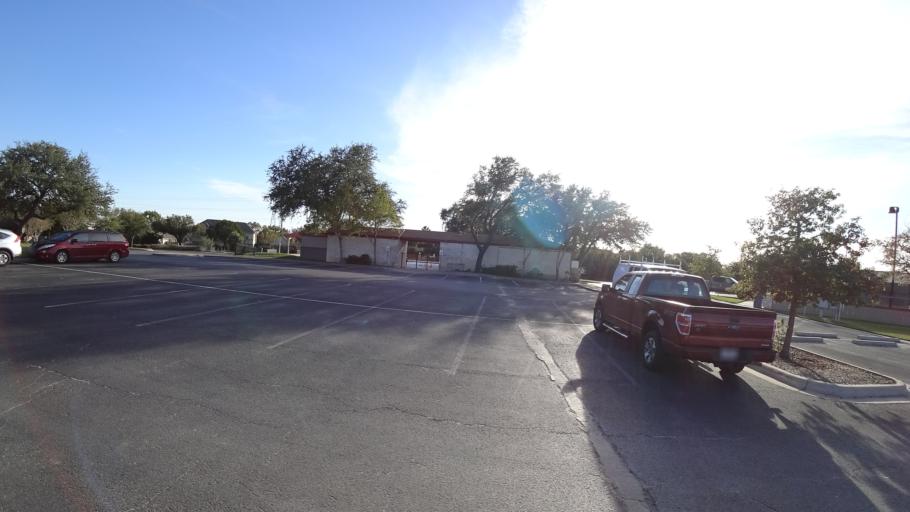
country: US
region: Texas
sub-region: Williamson County
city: Jollyville
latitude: 30.4029
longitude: -97.7674
